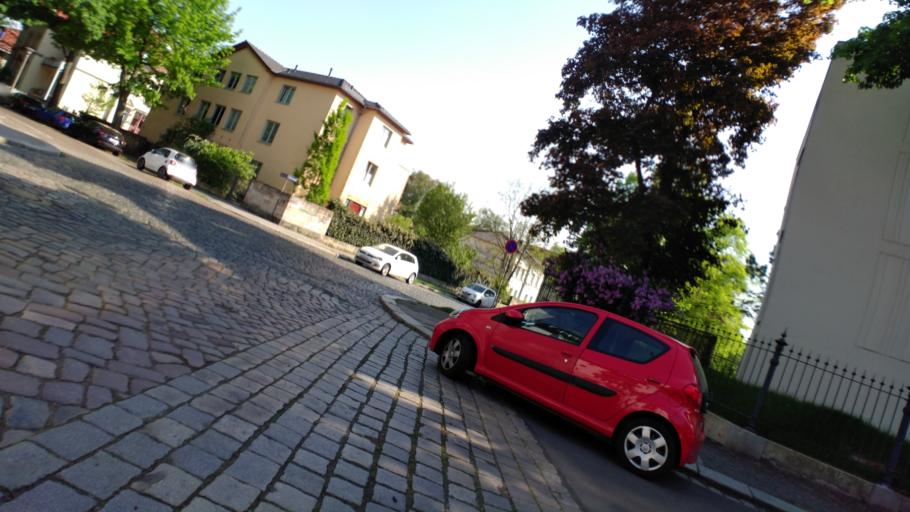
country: DE
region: Saxony
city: Albertstadt
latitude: 51.0703
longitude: 13.7660
